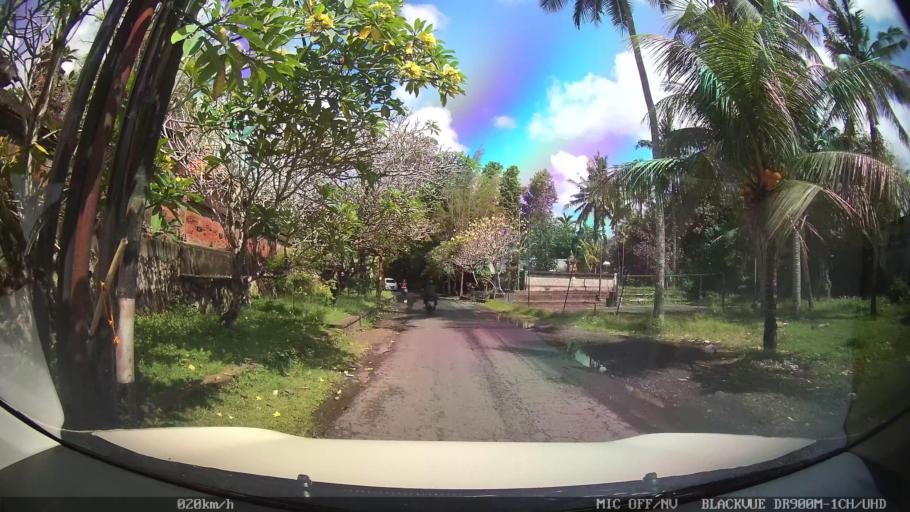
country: ID
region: Bali
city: Banjar Sedang
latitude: -8.5618
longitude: 115.2725
